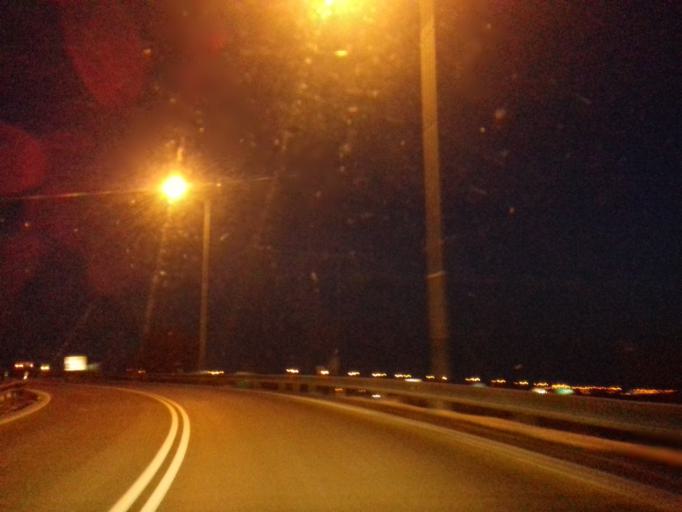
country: CZ
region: Central Bohemia
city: Cernosice
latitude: 50.0143
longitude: 14.3376
